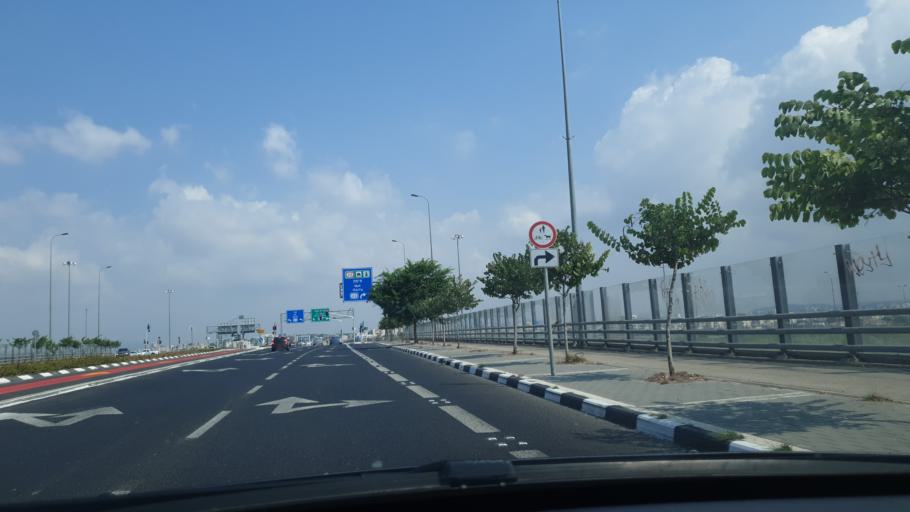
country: IL
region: Haifa
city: Qiryat Bialik
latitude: 32.8150
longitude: 35.0882
